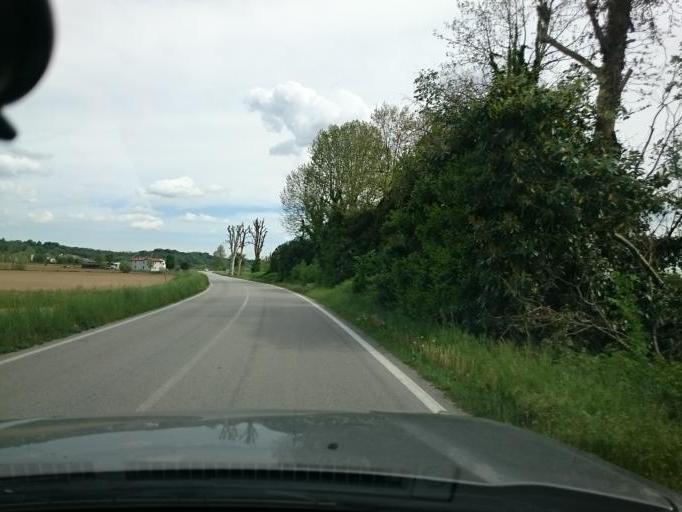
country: IT
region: Veneto
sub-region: Provincia di Vicenza
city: Montegalda
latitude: 45.4580
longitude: 11.6473
